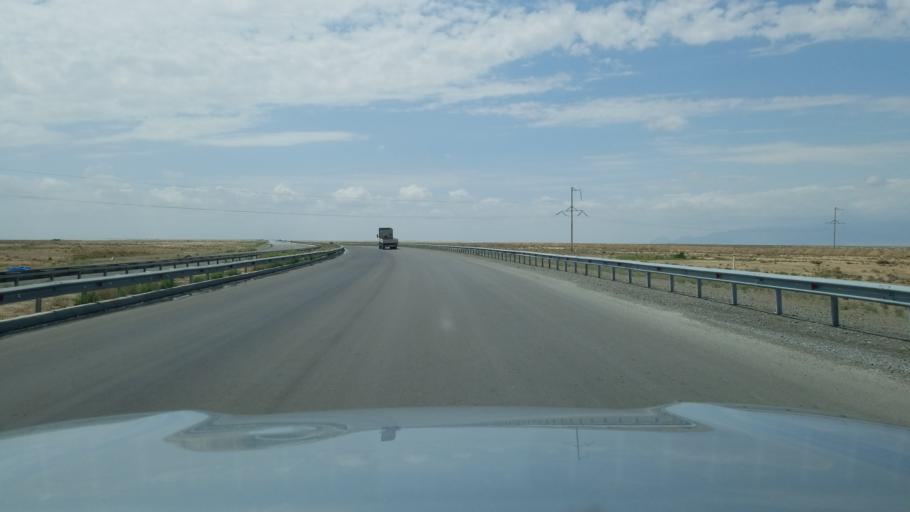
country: TM
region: Balkan
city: Gumdag
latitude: 39.2336
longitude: 54.7485
